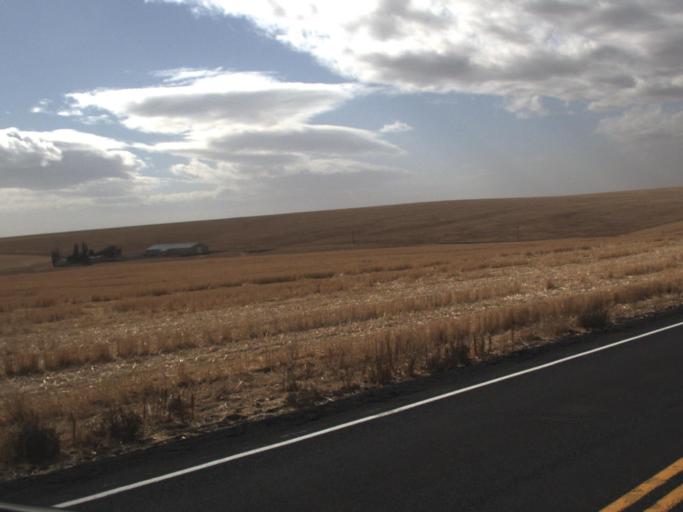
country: US
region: Washington
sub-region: Okanogan County
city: Coulee Dam
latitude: 47.6122
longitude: -118.7796
